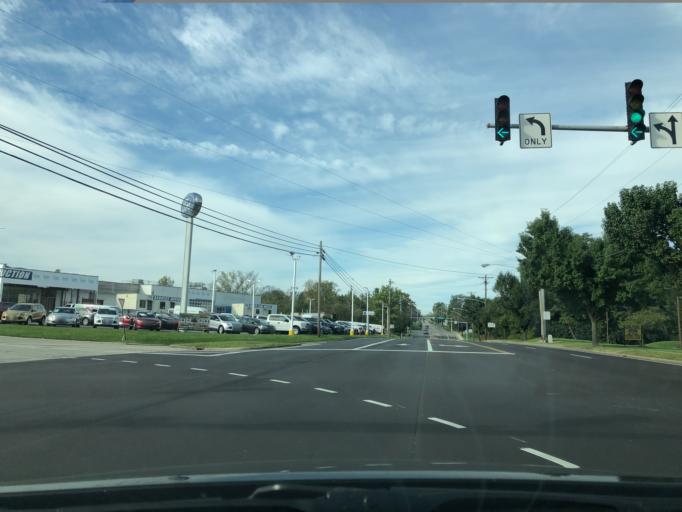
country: US
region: Ohio
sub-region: Hamilton County
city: Springdale
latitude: 39.2875
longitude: -84.4729
